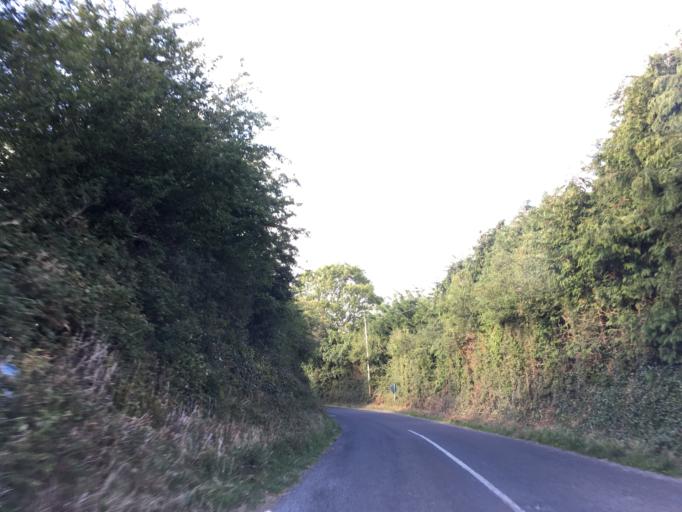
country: IE
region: Munster
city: Cahir
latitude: 52.2709
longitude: -7.9562
